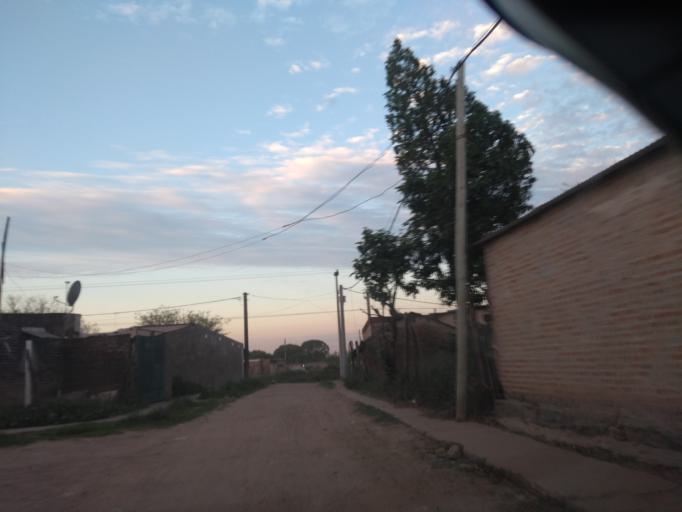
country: AR
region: Chaco
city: Fontana
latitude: -27.4104
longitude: -59.0524
